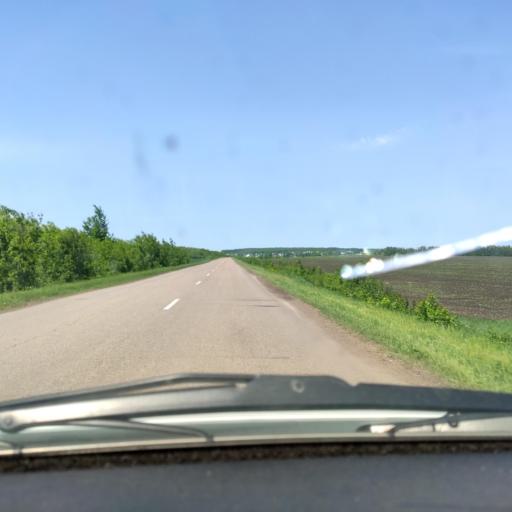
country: RU
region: Bashkortostan
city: Avdon
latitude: 54.5375
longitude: 55.6446
